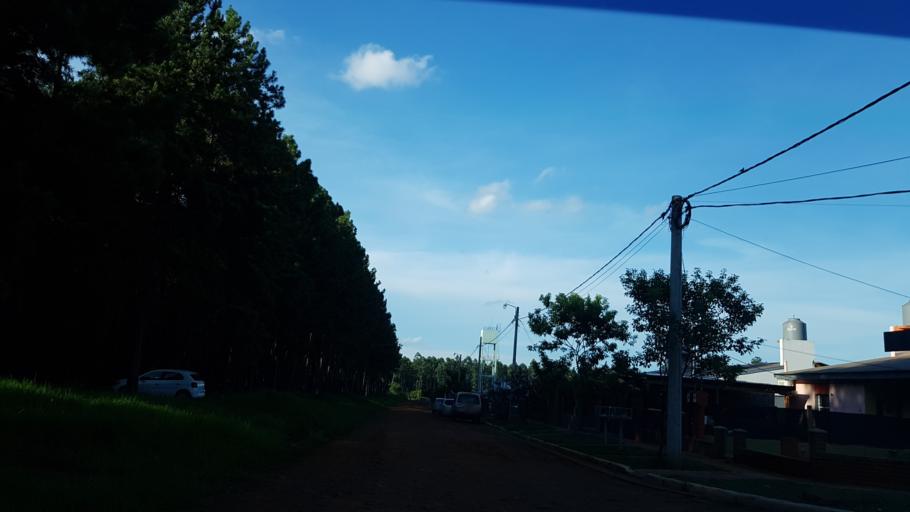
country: AR
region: Misiones
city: Puerto Libertad
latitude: -25.9188
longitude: -54.5908
